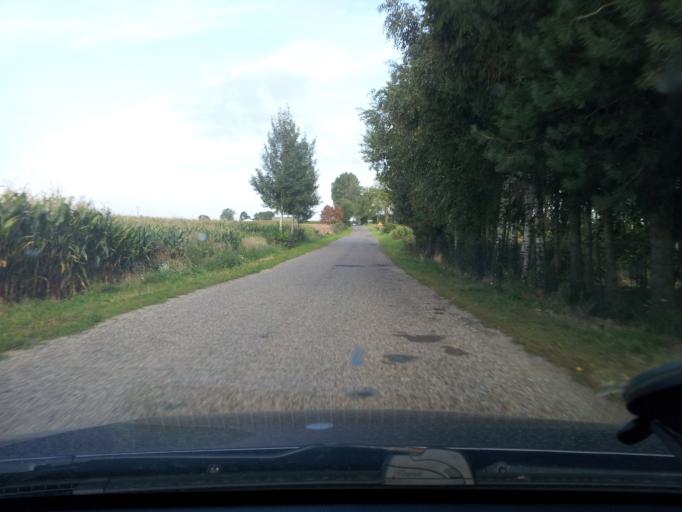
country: PL
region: Kujawsko-Pomorskie
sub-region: Powiat brodnicki
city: Bartniczka
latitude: 53.2076
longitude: 19.5844
